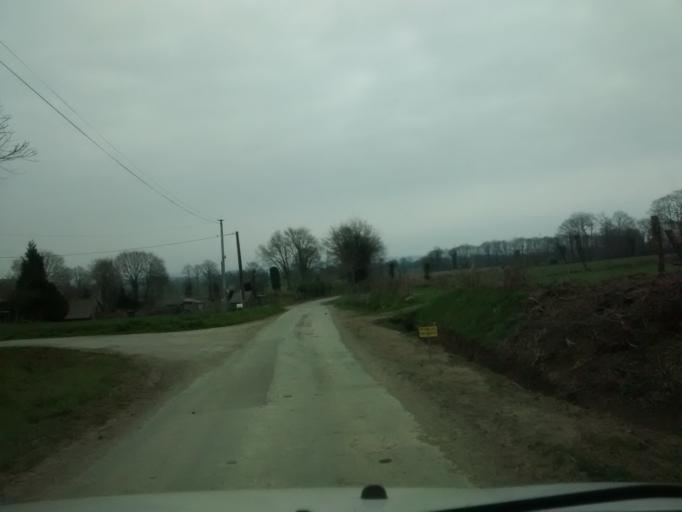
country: FR
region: Brittany
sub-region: Departement d'Ille-et-Vilaine
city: Bazouges-la-Perouse
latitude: 48.3830
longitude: -1.5644
